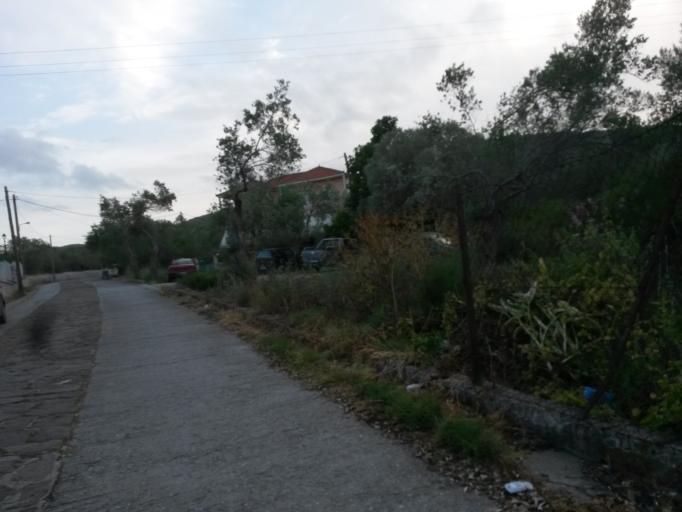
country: GR
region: North Aegean
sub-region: Nomos Lesvou
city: Pamfylla
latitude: 39.1737
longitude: 26.5025
